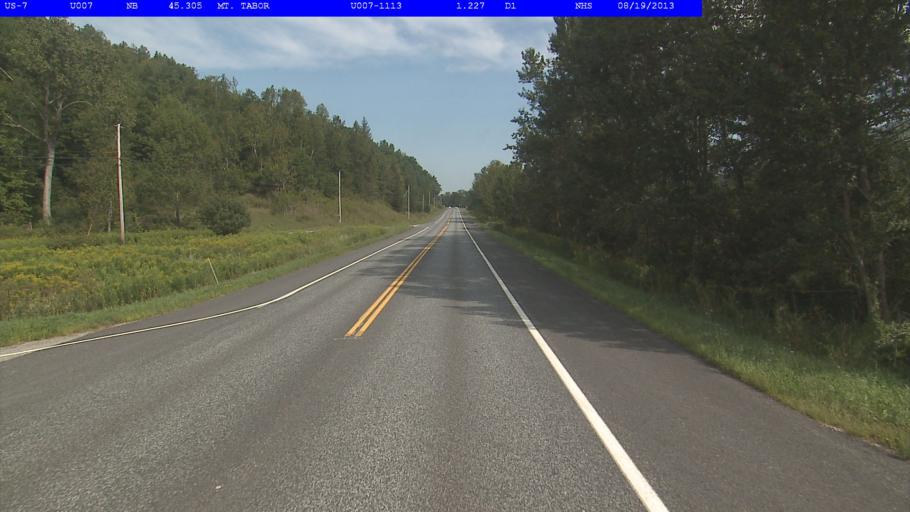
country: US
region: Vermont
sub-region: Bennington County
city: Manchester Center
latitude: 43.3225
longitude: -72.9911
